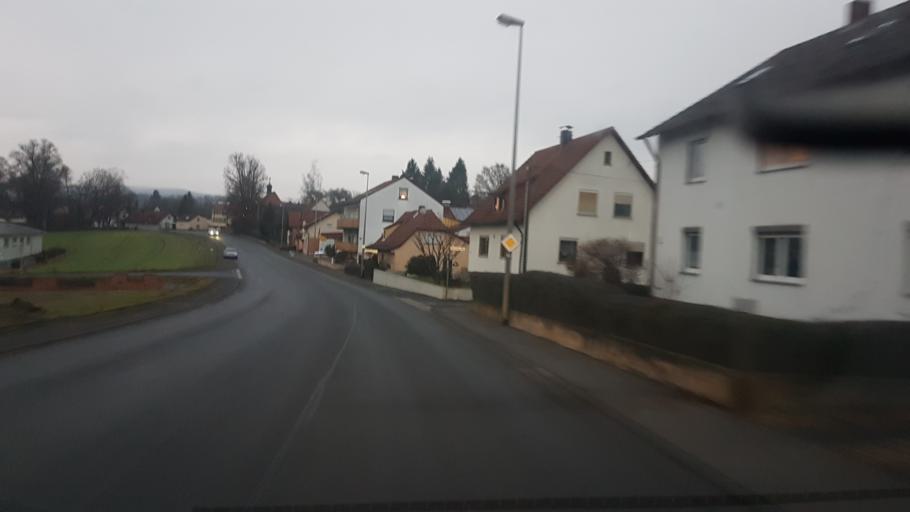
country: DE
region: Bavaria
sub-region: Regierungsbezirk Unterfranken
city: Pfarrweisach
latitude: 50.1687
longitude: 10.7195
